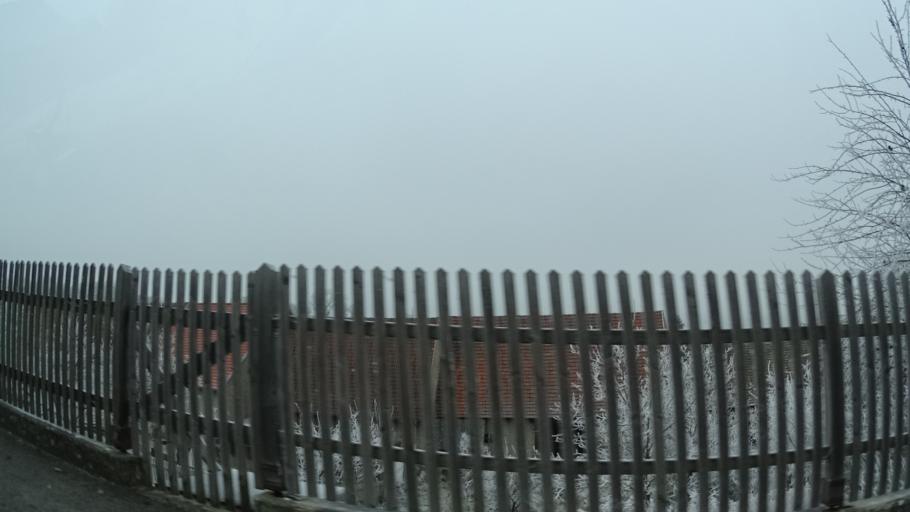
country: DE
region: Bavaria
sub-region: Regierungsbezirk Unterfranken
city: Oberelsbach
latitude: 50.4212
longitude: 10.0934
